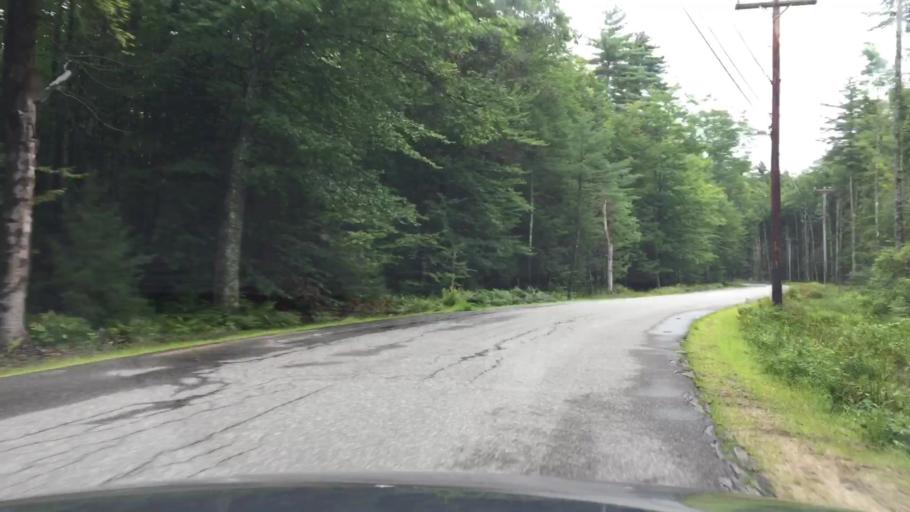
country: US
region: New Hampshire
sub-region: Carroll County
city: Center Harbor
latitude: 43.7283
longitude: -71.4851
